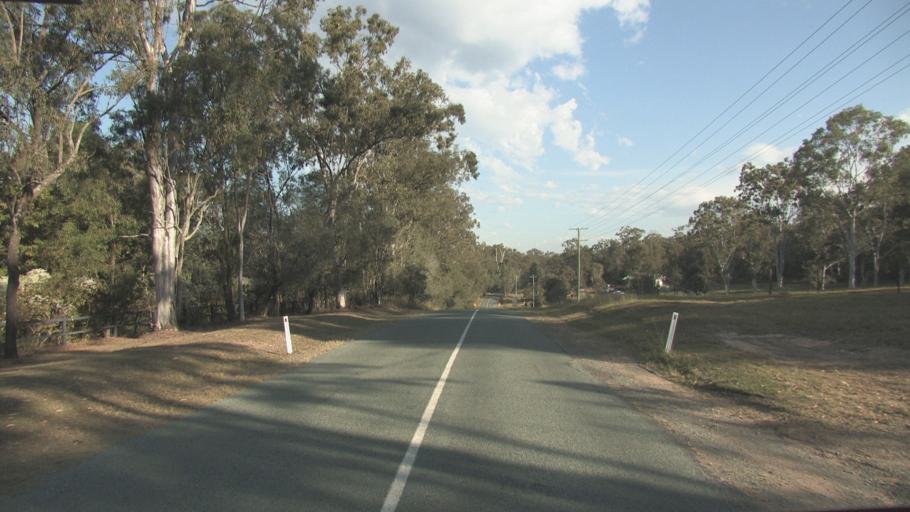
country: AU
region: Queensland
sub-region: Gold Coast
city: Ormeau Hills
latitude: -27.8346
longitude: 153.1693
